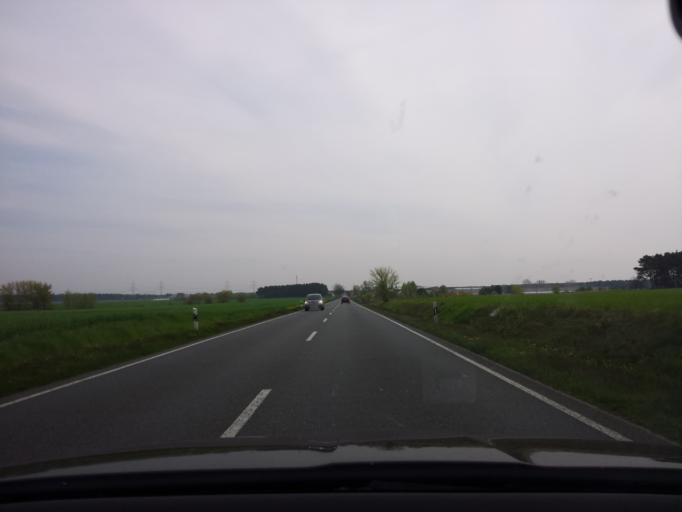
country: DE
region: Brandenburg
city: Luckau
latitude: 51.8899
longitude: 13.7910
